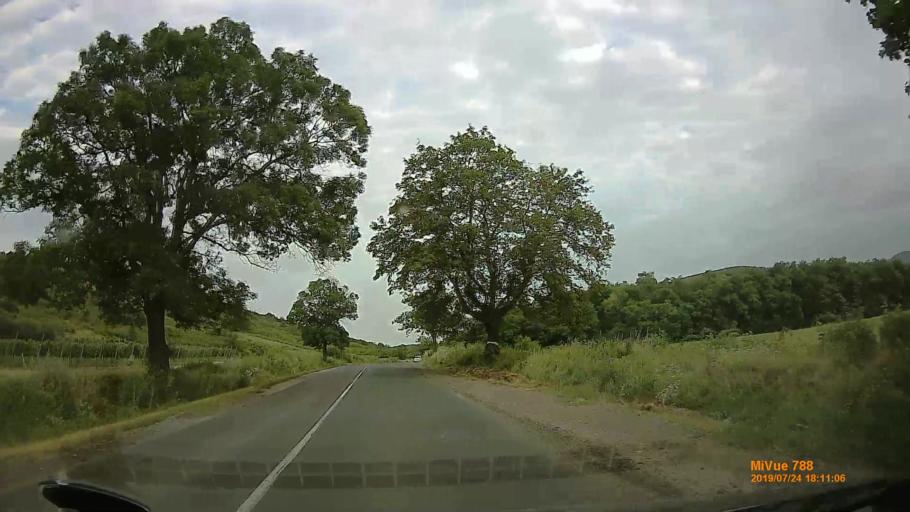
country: HU
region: Borsod-Abauj-Zemplen
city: Abaujszanto
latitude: 48.2512
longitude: 21.1962
